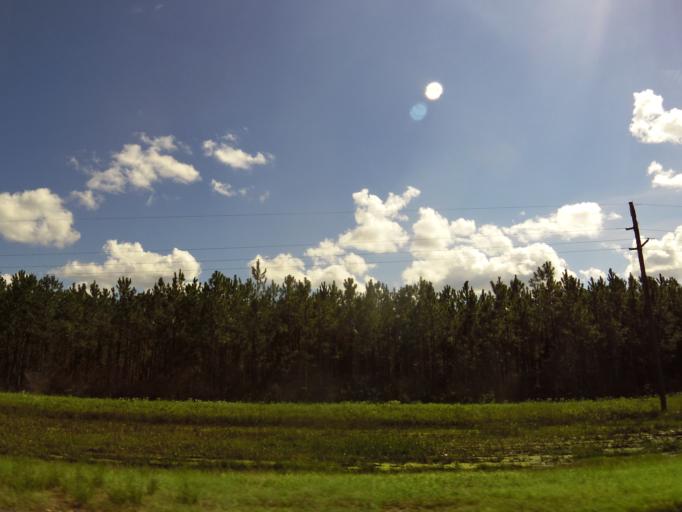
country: US
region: Florida
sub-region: Hamilton County
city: Jasper
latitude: 30.6781
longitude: -82.6154
